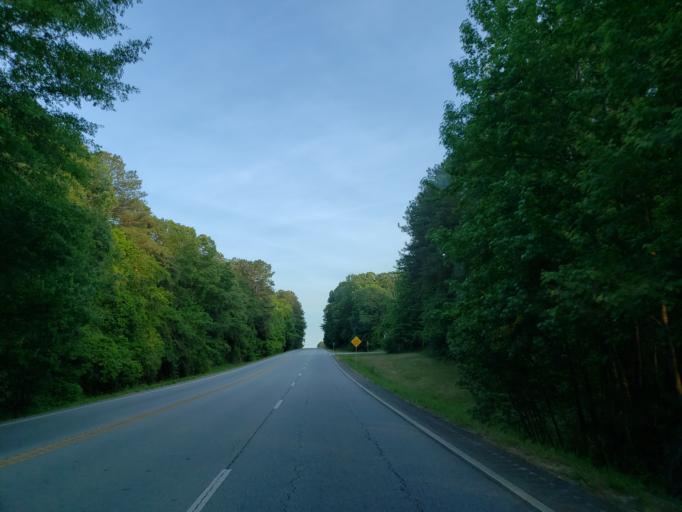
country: US
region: Georgia
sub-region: Coweta County
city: Newnan
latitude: 33.4652
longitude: -84.8936
